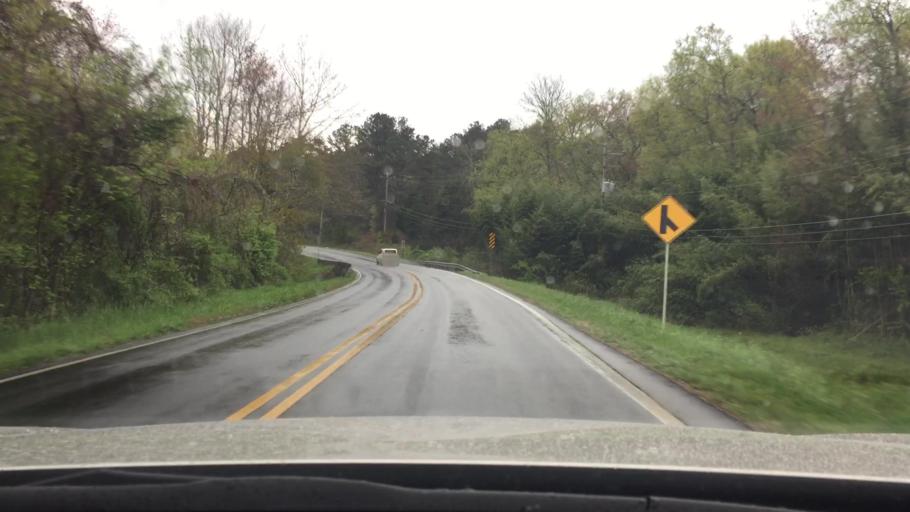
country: US
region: Georgia
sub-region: Catoosa County
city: Lakeview
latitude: 34.9758
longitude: -85.2399
